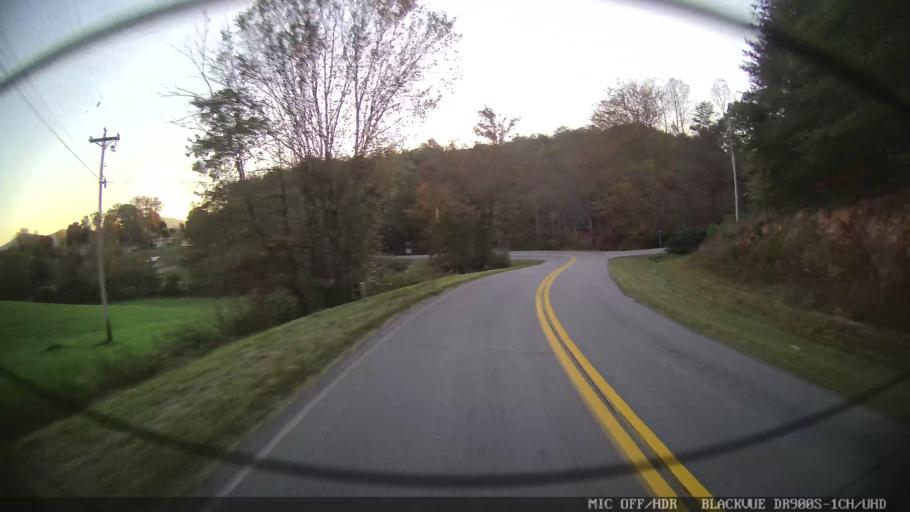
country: US
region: Georgia
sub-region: Union County
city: Blairsville
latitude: 34.8569
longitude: -83.8966
